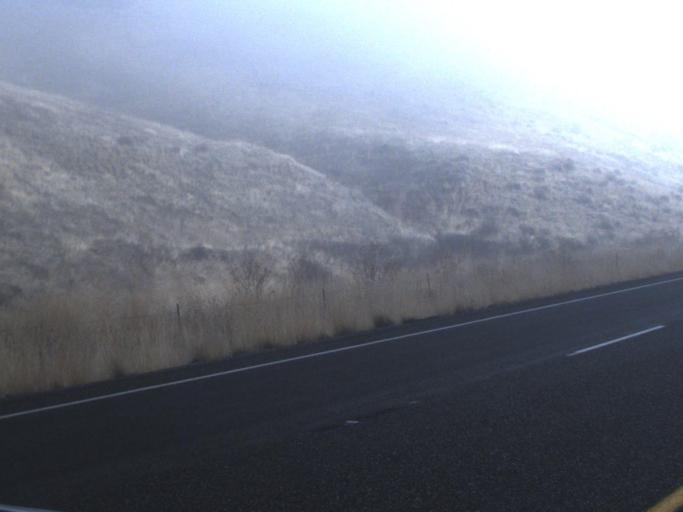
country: US
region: Washington
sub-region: Garfield County
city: Pomeroy
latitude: 46.4355
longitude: -117.3462
